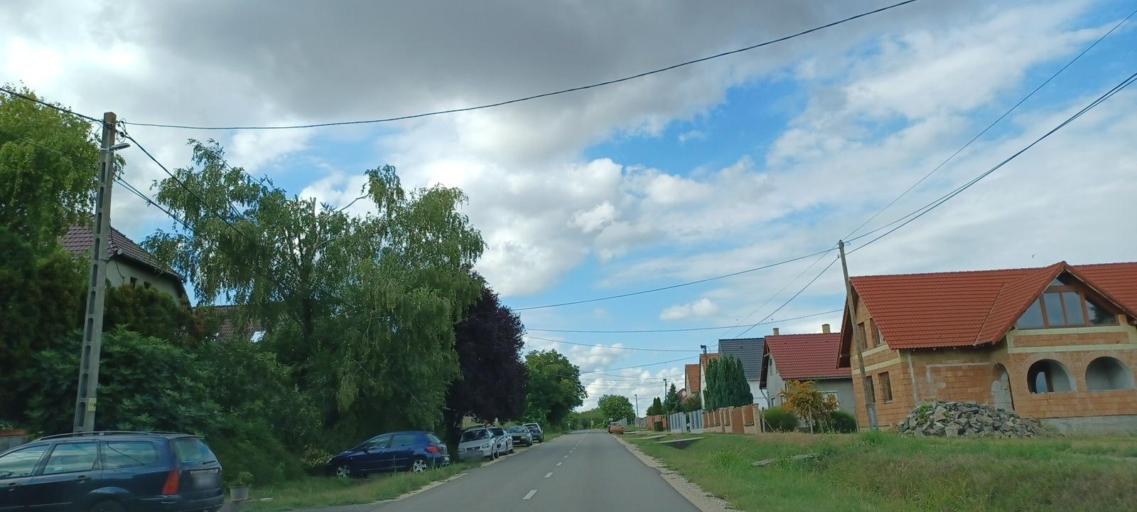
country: HU
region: Tolna
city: Szentgalpuszta
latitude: 46.4050
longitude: 18.6167
